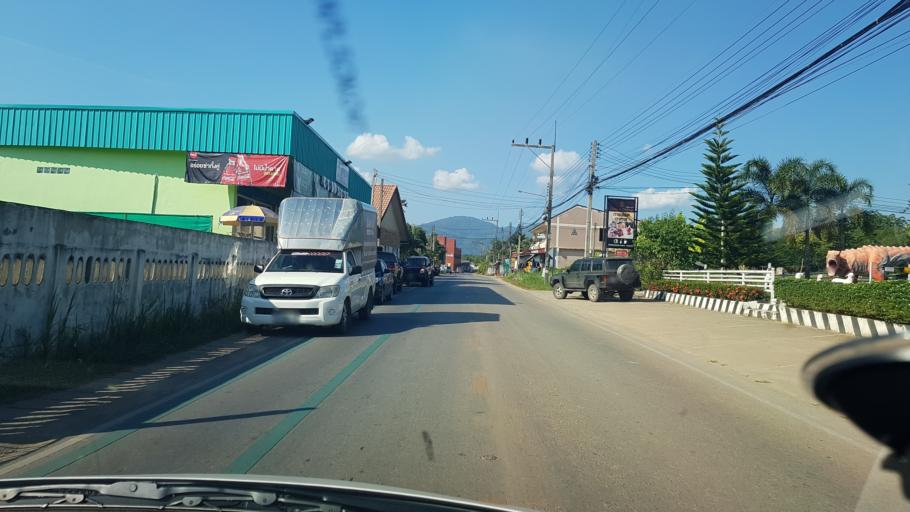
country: TH
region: Chiang Rai
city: Chiang Rai
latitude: 19.9479
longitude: 99.8102
